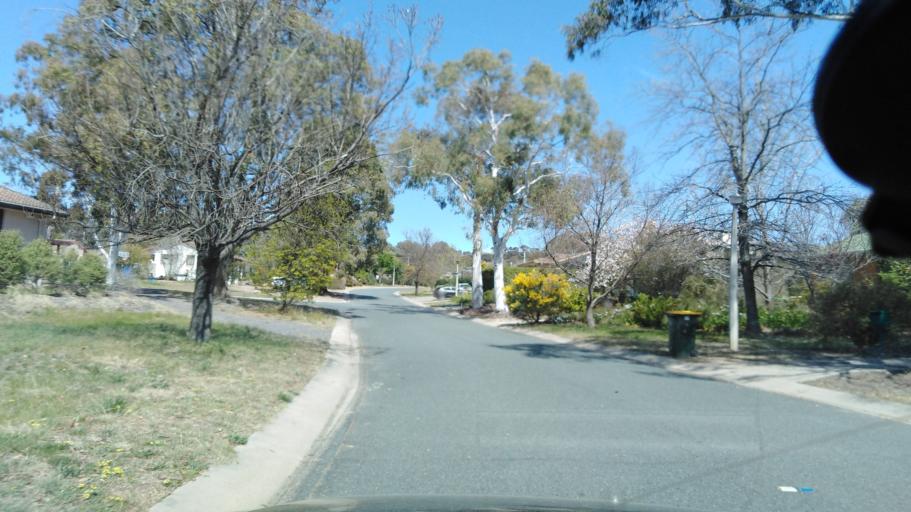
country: AU
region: Australian Capital Territory
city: Macquarie
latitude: -35.3478
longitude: 149.0318
